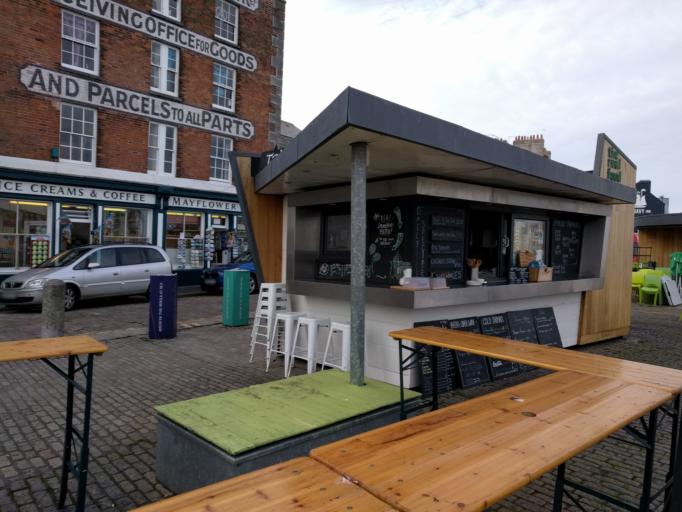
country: GB
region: England
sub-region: Plymouth
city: Plymouth
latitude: 50.3665
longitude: -4.1341
